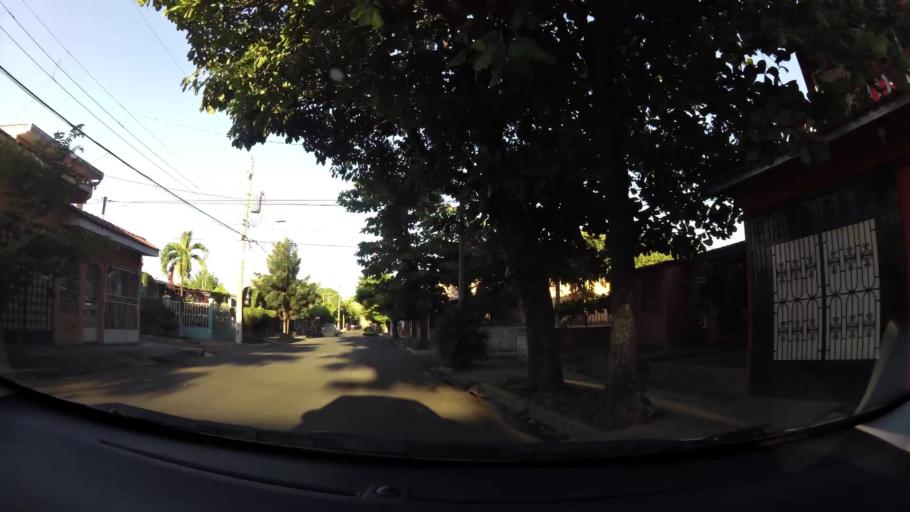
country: SV
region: Sonsonate
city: San Antonio del Monte
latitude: 13.7063
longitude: -89.7319
